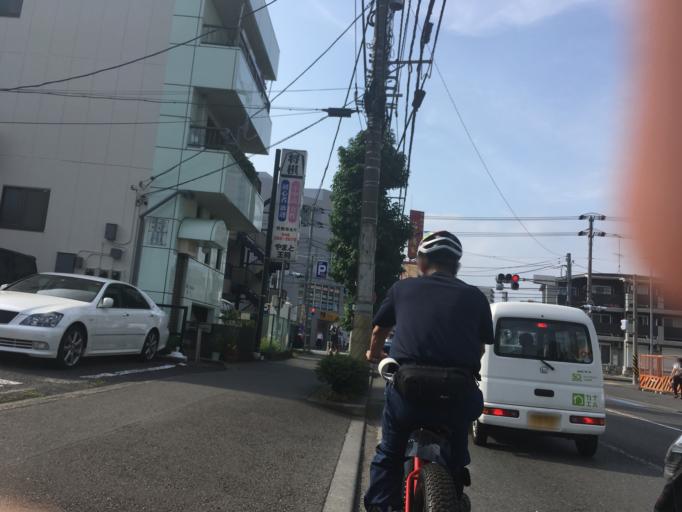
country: JP
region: Kanagawa
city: Minami-rinkan
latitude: 35.4751
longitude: 139.4621
